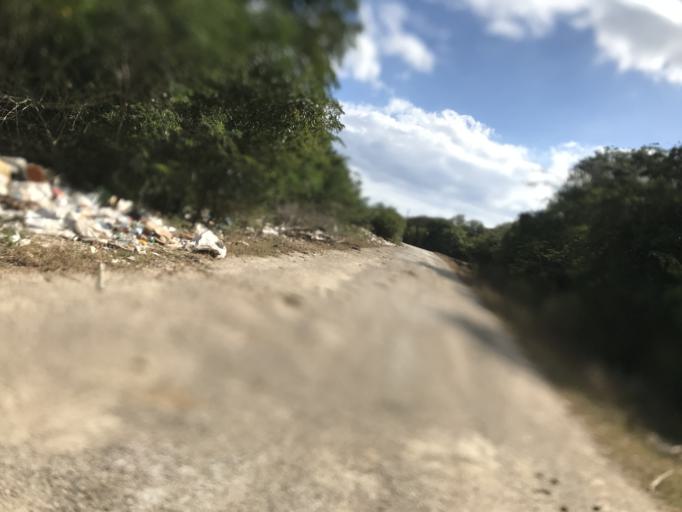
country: CU
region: Cienfuegos
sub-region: Municipio de Aguada de Pasajeros
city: Aguada de Pasajeros
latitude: 22.0728
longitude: -81.0360
